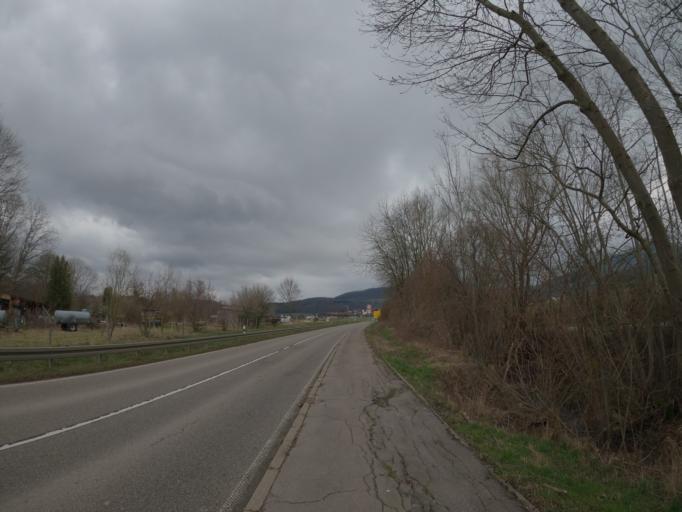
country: DE
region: Baden-Wuerttemberg
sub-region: Regierungsbezirk Stuttgart
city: Schlat
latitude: 48.6609
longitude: 9.7038
